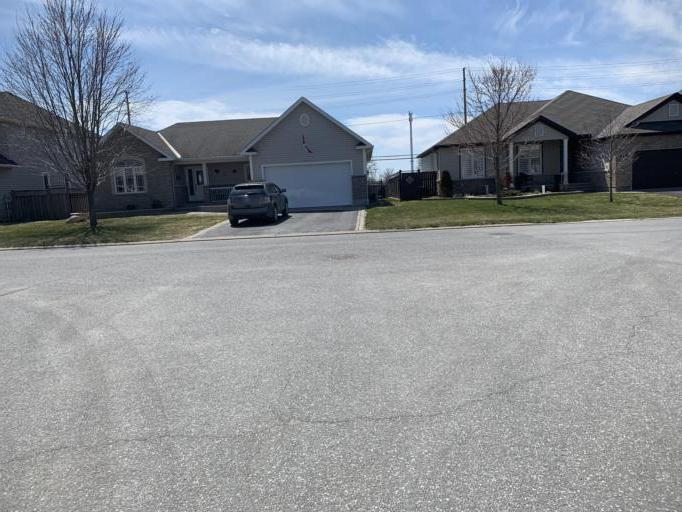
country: CA
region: Ontario
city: Bells Corners
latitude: 45.1982
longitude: -75.8390
